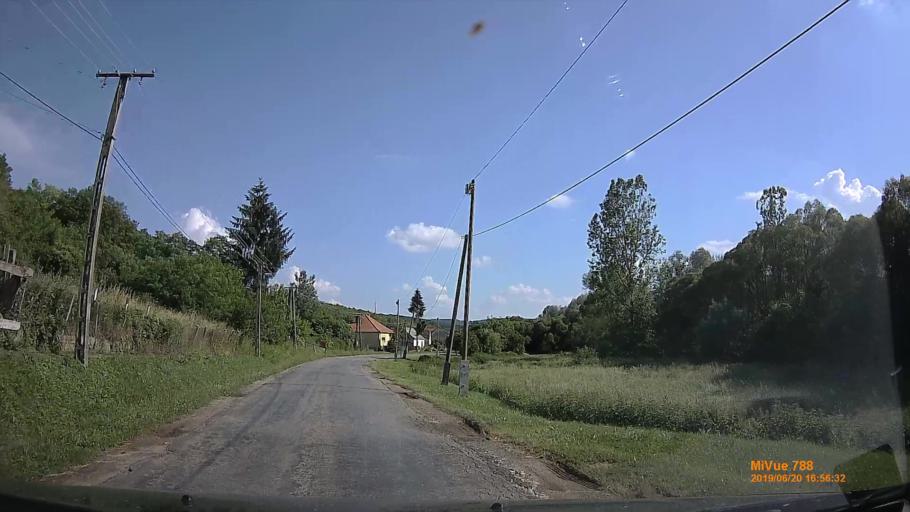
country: HU
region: Baranya
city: Buekkoesd
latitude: 46.1489
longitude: 18.0601
